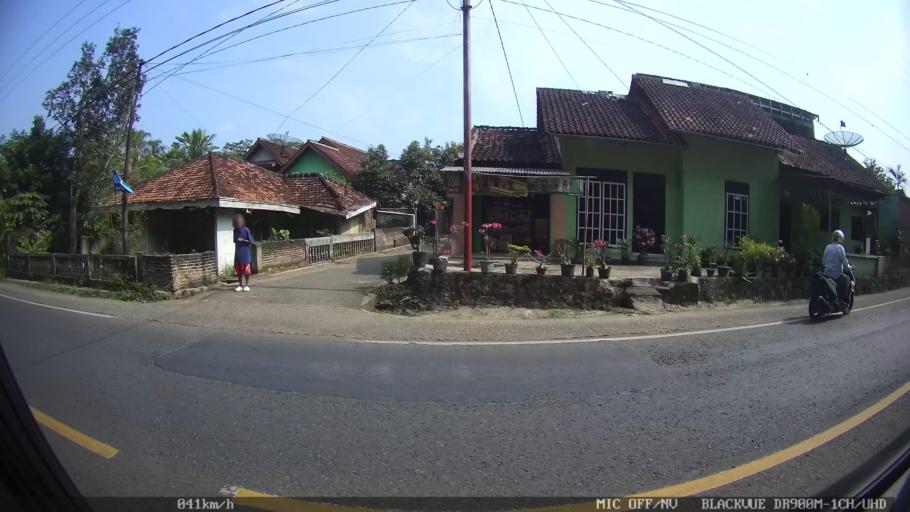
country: ID
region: Lampung
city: Gedongtataan
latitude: -5.3801
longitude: 105.1186
